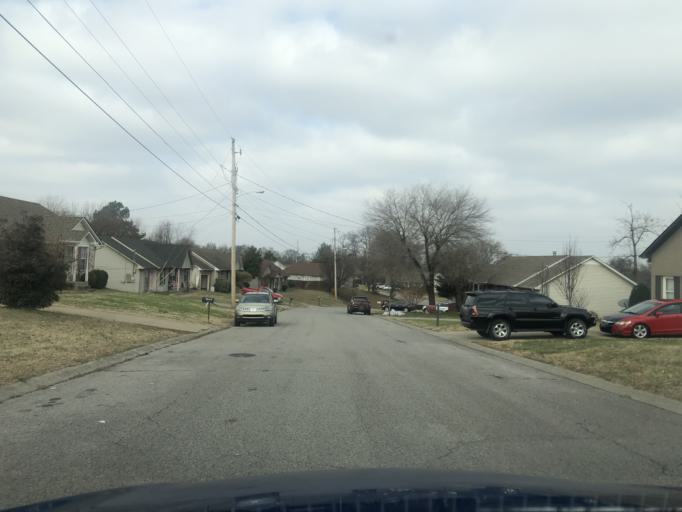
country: US
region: Tennessee
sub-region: Davidson County
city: Oak Hill
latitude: 36.0900
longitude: -86.7072
